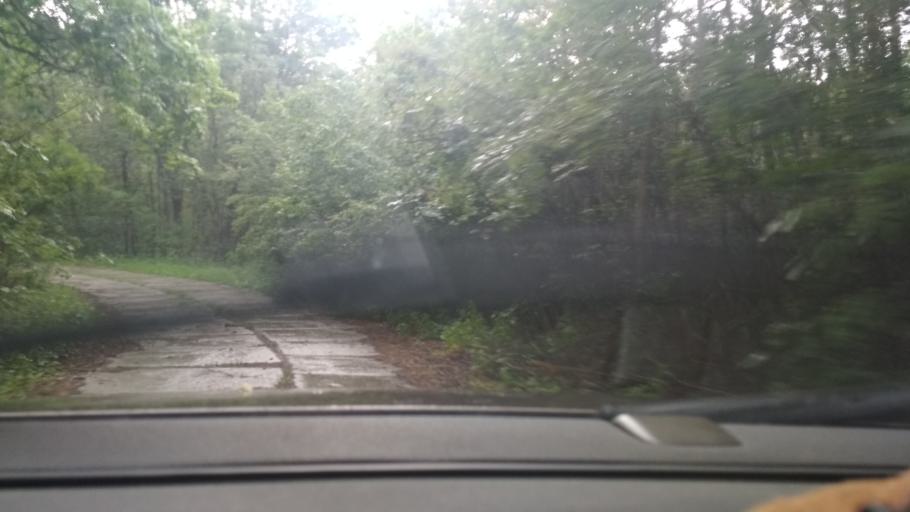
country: MD
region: Singerei
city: Biruinta
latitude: 47.7511
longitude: 28.1410
